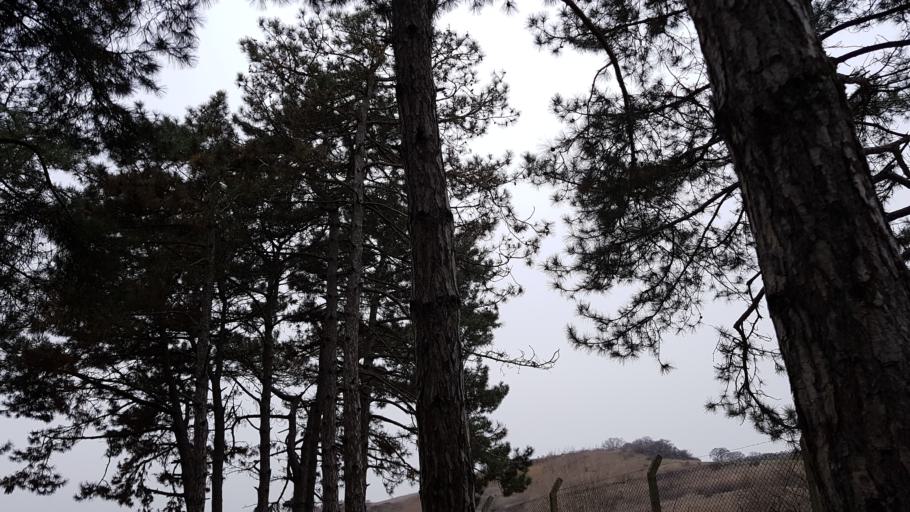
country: TR
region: Tekirdag
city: Muratli
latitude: 41.1844
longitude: 27.4770
